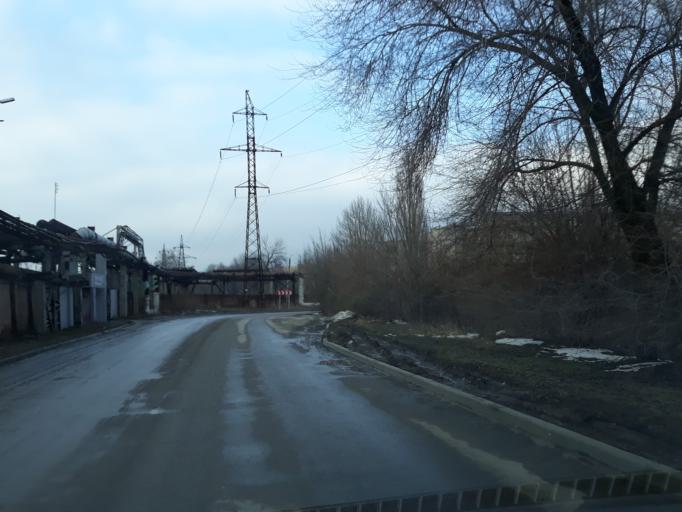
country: RU
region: Rostov
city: Taganrog
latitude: 47.2522
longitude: 38.9038
